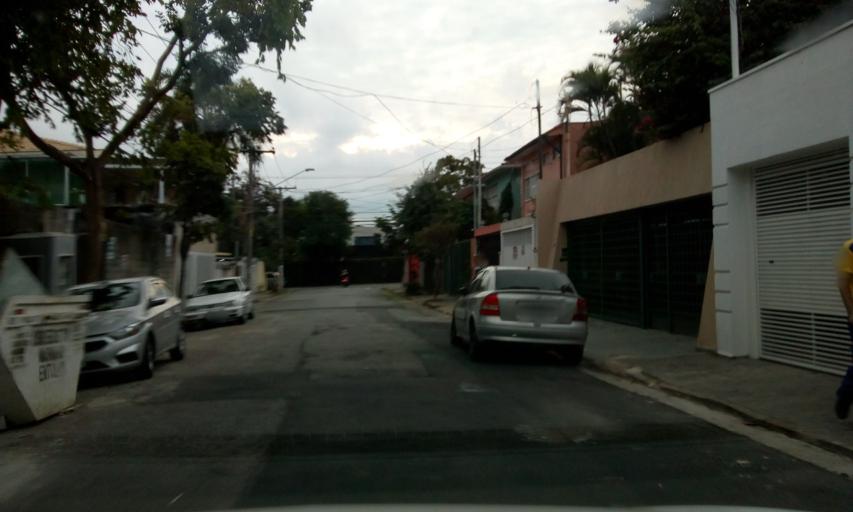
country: BR
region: Sao Paulo
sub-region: Sao Paulo
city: Sao Paulo
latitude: -23.6069
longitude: -46.6841
